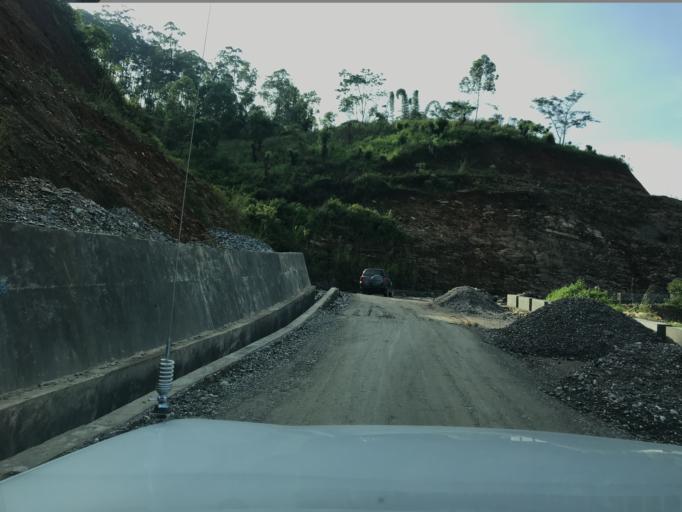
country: TL
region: Aileu
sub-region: Aileu Villa
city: Aileu
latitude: -8.6558
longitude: 125.5273
